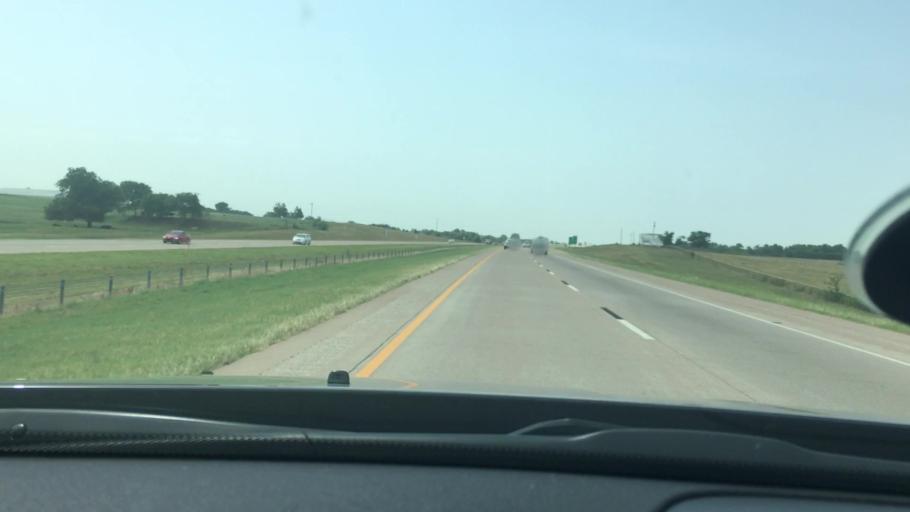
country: US
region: Oklahoma
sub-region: Garvin County
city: Wynnewood
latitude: 34.6626
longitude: -97.2223
